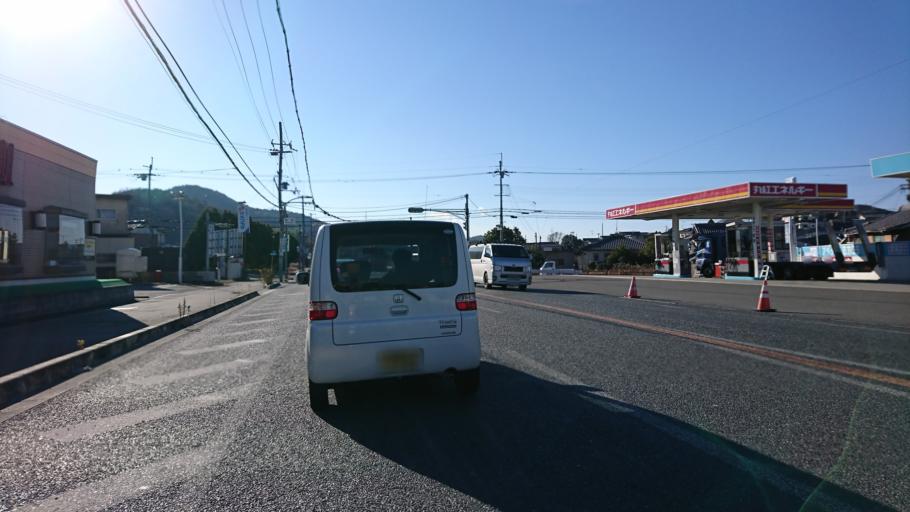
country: JP
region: Hyogo
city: Kakogawacho-honmachi
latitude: 34.8151
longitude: 134.8357
